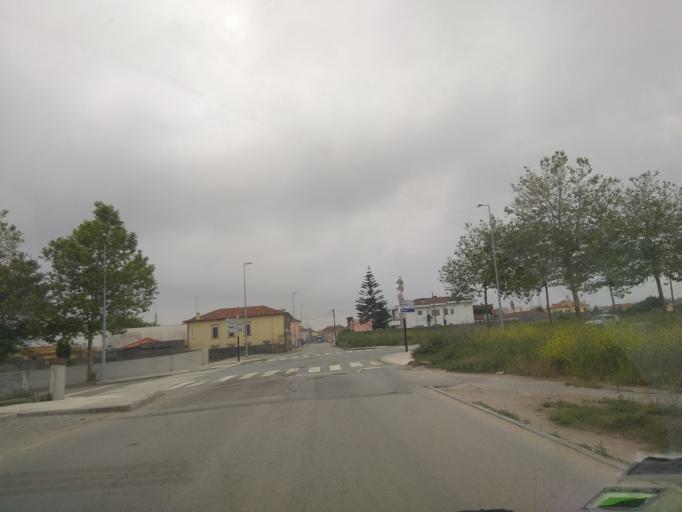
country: PT
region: Porto
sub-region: Matosinhos
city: Guifoes
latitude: 41.1980
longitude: -8.6647
